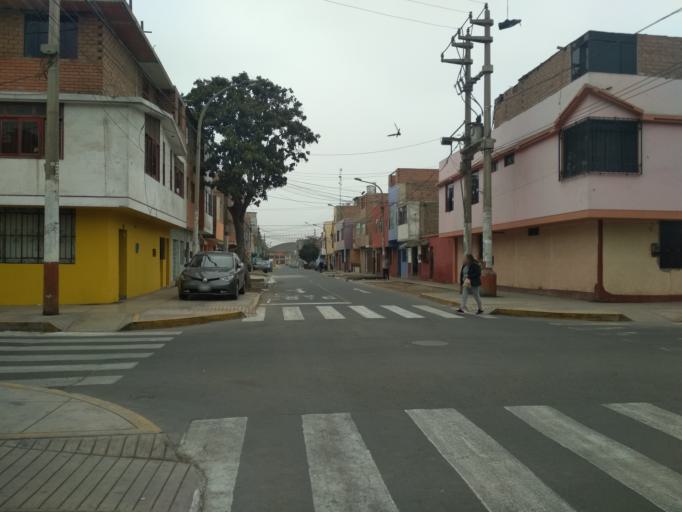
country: PE
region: Callao
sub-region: Callao
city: Callao
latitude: -12.0533
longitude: -77.1018
